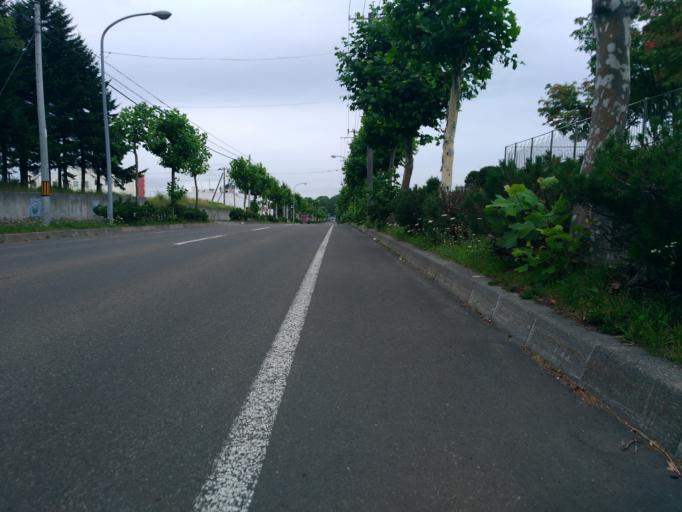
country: JP
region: Hokkaido
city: Ebetsu
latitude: 43.0663
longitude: 141.5024
